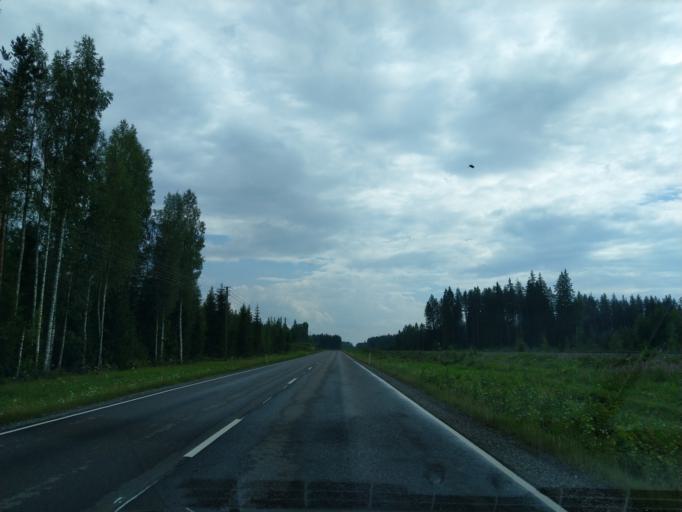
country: FI
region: South Karelia
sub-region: Imatra
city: Parikkala
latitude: 61.6319
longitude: 29.4305
